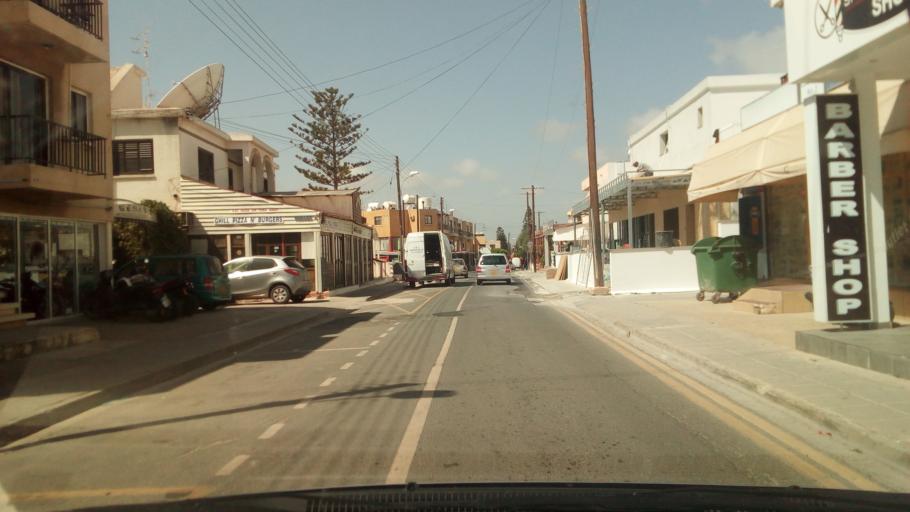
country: CY
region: Ammochostos
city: Ayia Napa
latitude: 34.9916
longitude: 33.9971
